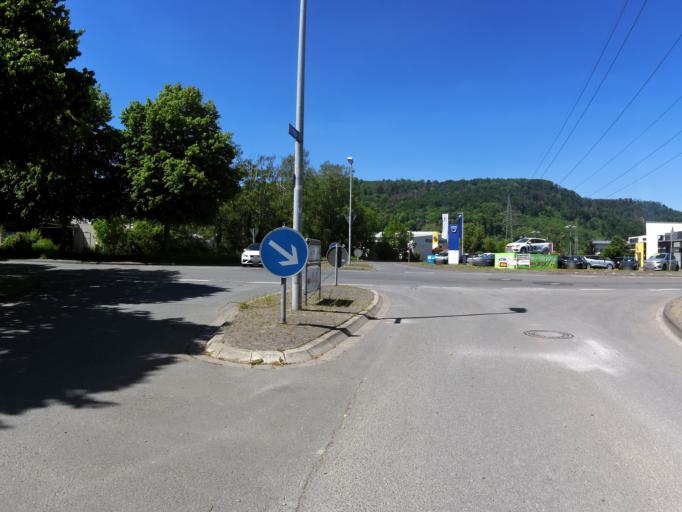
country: DE
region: North Rhine-Westphalia
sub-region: Regierungsbezirk Detmold
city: Hoexter
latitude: 51.7837
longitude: 9.3960
